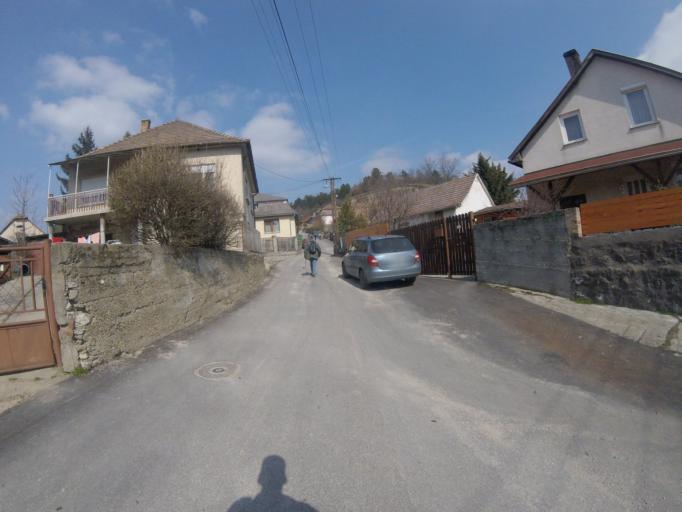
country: HU
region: Komarom-Esztergom
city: Nyergesujfalu
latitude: 47.7592
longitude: 18.5558
